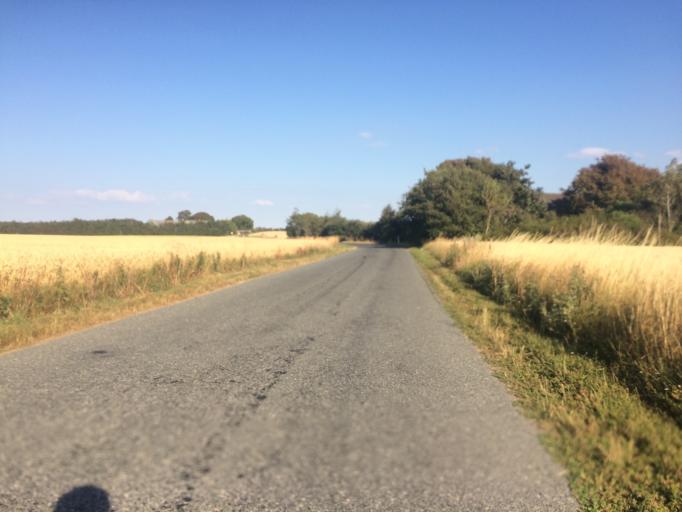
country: DK
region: Central Jutland
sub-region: Holstebro Kommune
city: Vinderup
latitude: 56.5872
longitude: 8.7701
